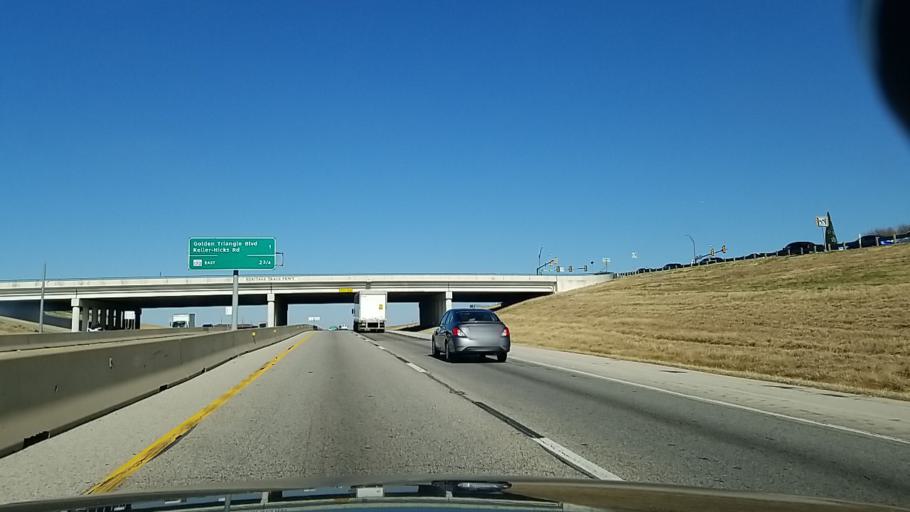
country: US
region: Texas
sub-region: Tarrant County
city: Blue Mound
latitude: 32.9134
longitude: -97.3171
